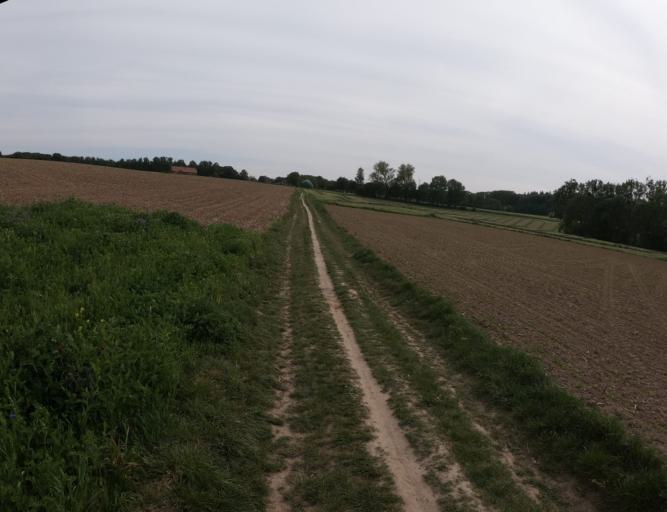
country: BE
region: Flanders
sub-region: Provincie Vlaams-Brabant
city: Beersel
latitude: 50.7466
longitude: 4.2993
